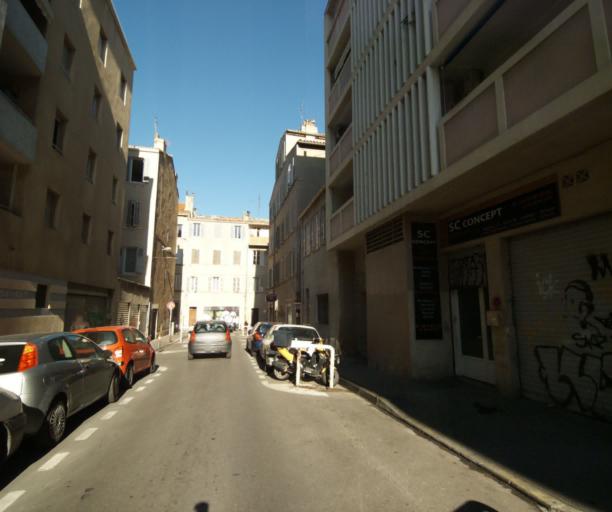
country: FR
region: Provence-Alpes-Cote d'Azur
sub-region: Departement des Bouches-du-Rhone
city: Marseille 05
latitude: 43.2875
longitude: 5.3944
